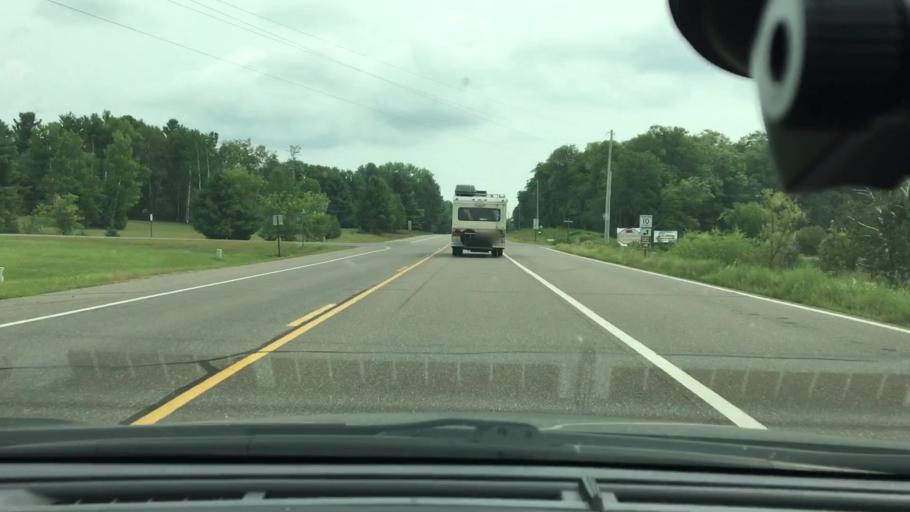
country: US
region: Minnesota
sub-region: Crow Wing County
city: Crosby
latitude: 46.4103
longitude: -93.8477
